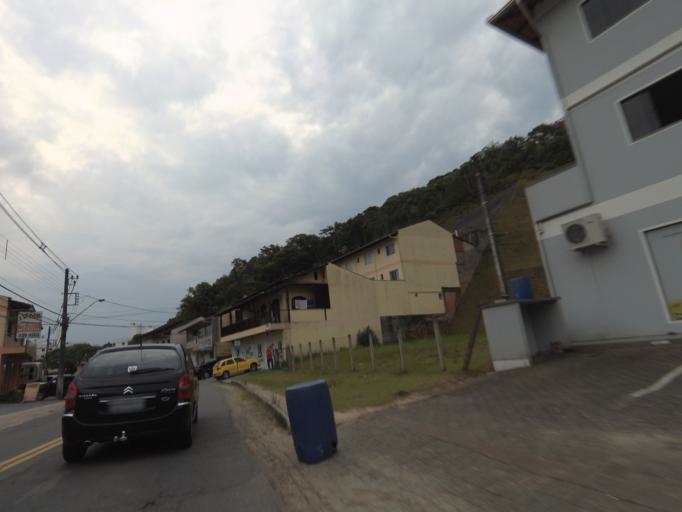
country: BR
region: Santa Catarina
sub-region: Blumenau
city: Blumenau
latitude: -26.8747
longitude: -49.0523
